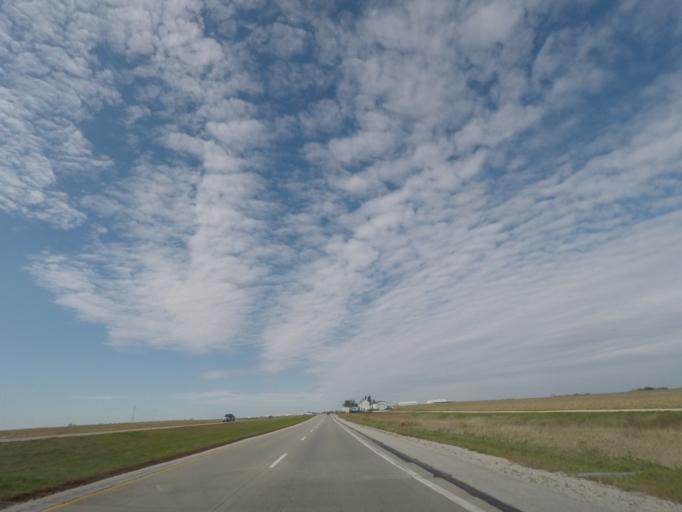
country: US
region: Iowa
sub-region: Story County
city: Ames
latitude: 42.0233
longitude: -93.7426
